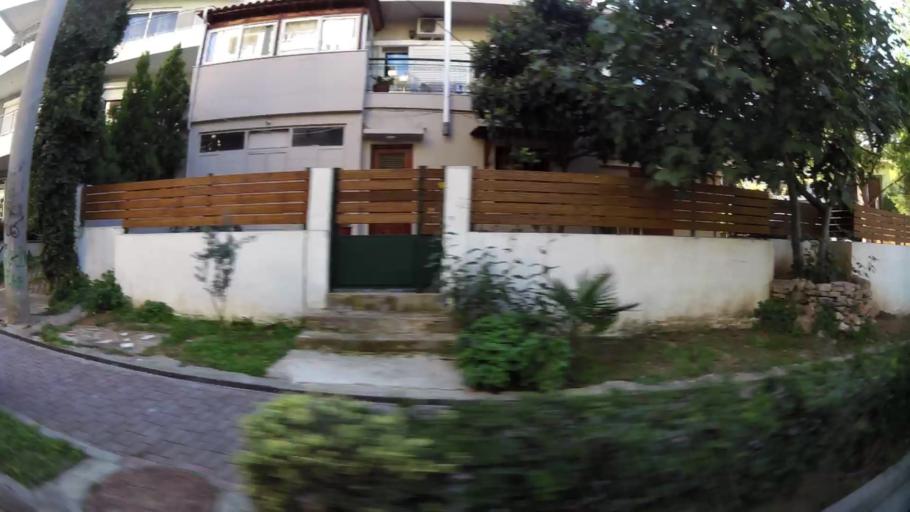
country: GR
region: Attica
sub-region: Nomarchia Athinas
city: Nea Erythraia
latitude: 38.0922
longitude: 23.8170
